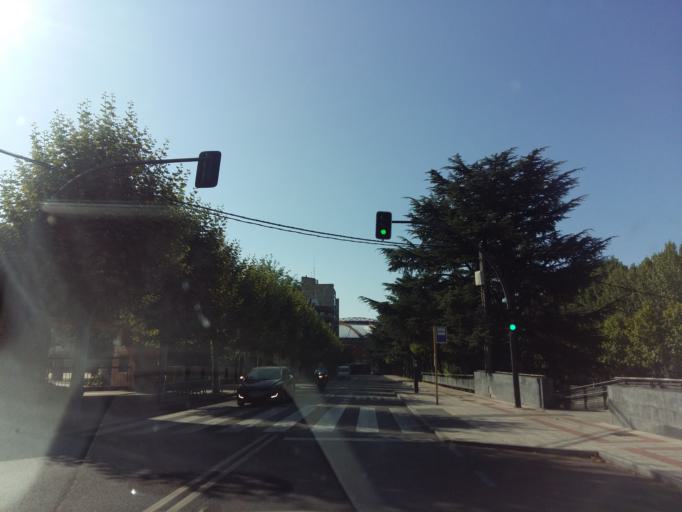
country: ES
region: Castille and Leon
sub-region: Provincia de Leon
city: Leon
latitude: 42.5901
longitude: -5.5742
